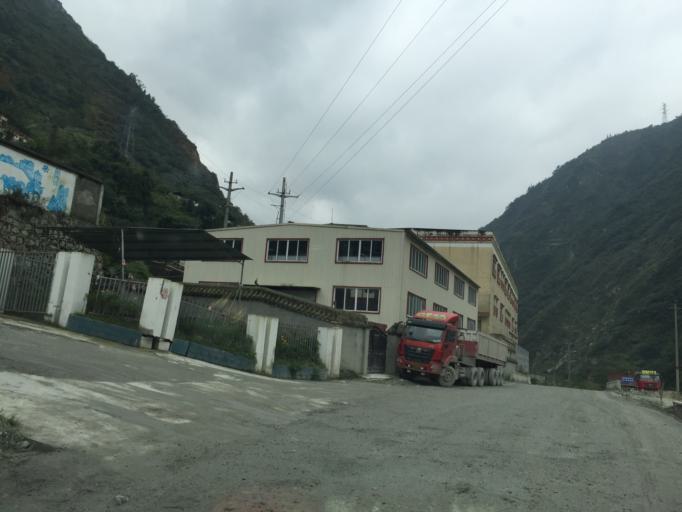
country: CN
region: Sichuan
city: Guangsheng
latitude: 31.0802
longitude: 103.4849
